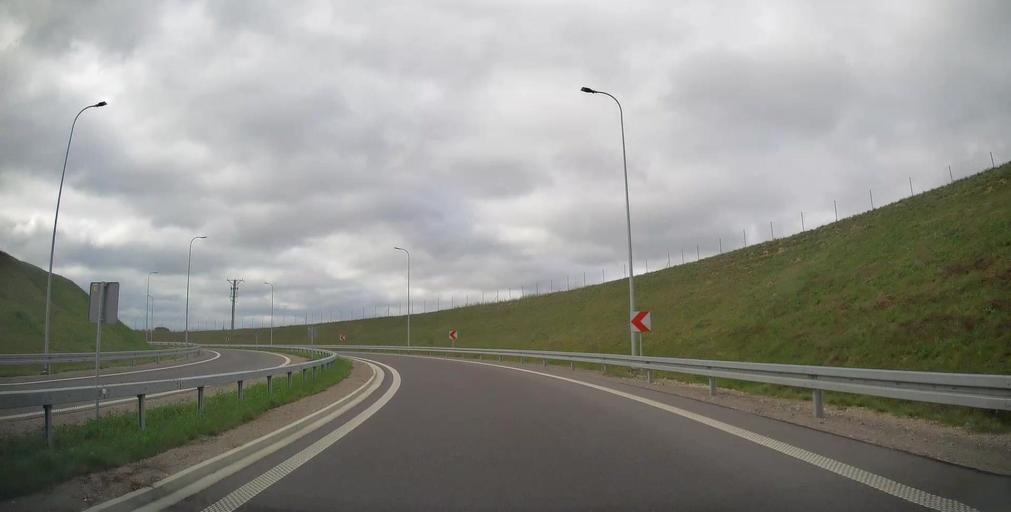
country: PL
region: Lesser Poland Voivodeship
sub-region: Powiat krakowski
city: Michalowice
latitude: 50.2079
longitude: 20.0149
